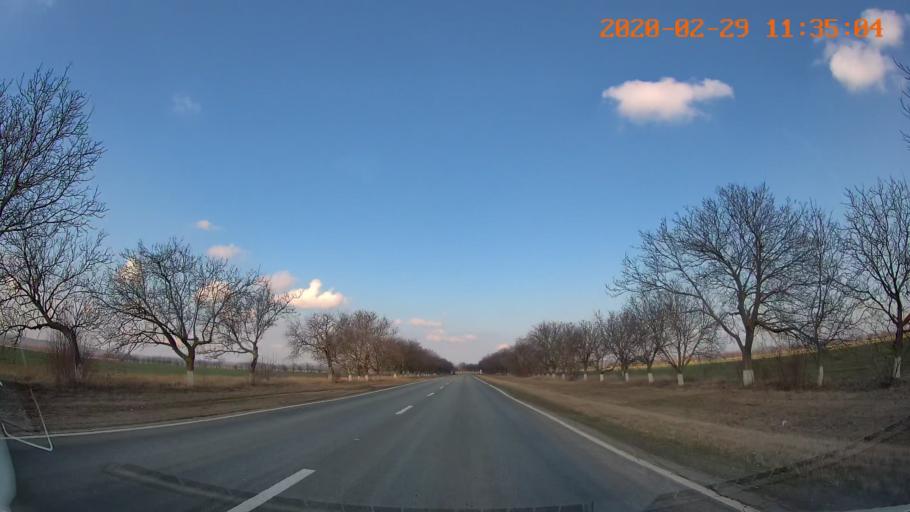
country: MD
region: Rezina
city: Saharna
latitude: 47.5749
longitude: 29.0669
